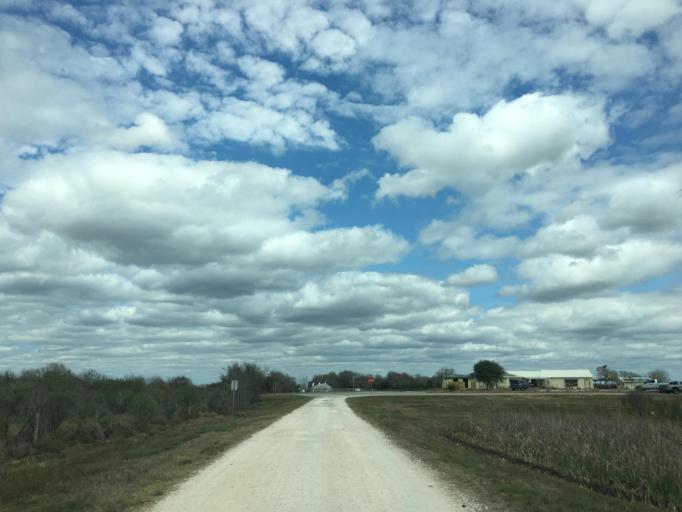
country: US
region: Texas
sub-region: Brazoria County
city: Oyster Creek
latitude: 29.0586
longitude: -95.2687
